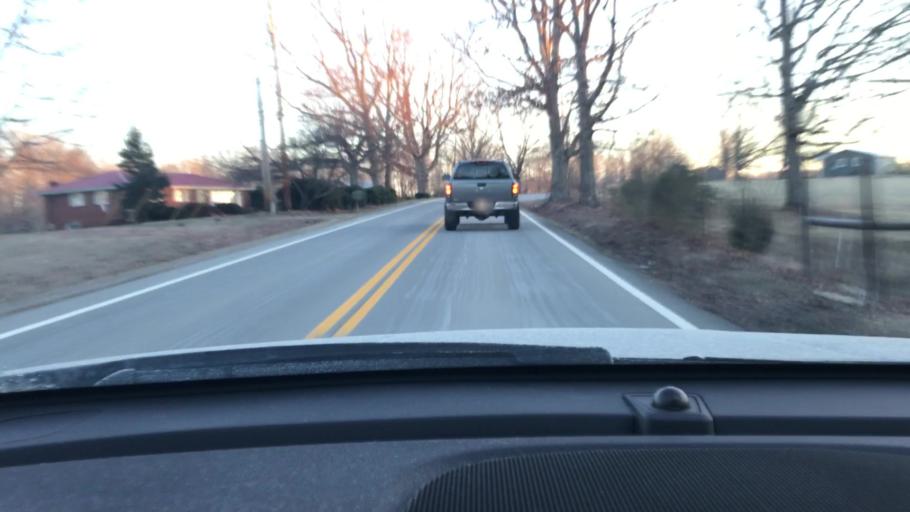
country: US
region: Tennessee
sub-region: Dickson County
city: Charlotte
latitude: 36.2242
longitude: -87.2587
